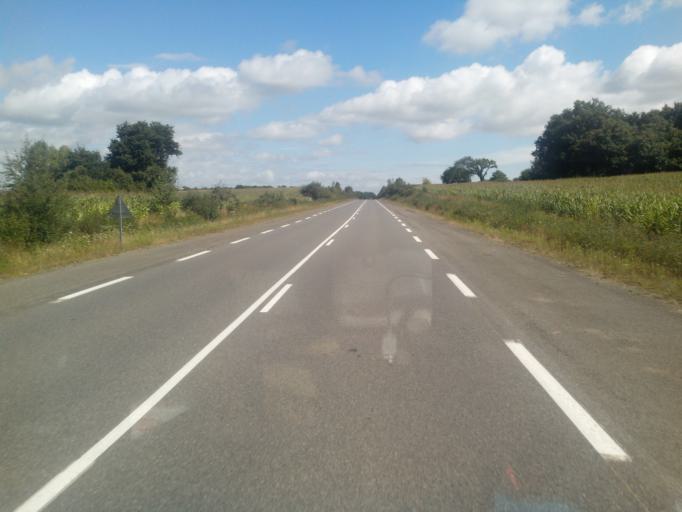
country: FR
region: Brittany
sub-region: Departement du Morbihan
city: Limerzel
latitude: 47.6162
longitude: -2.4002
